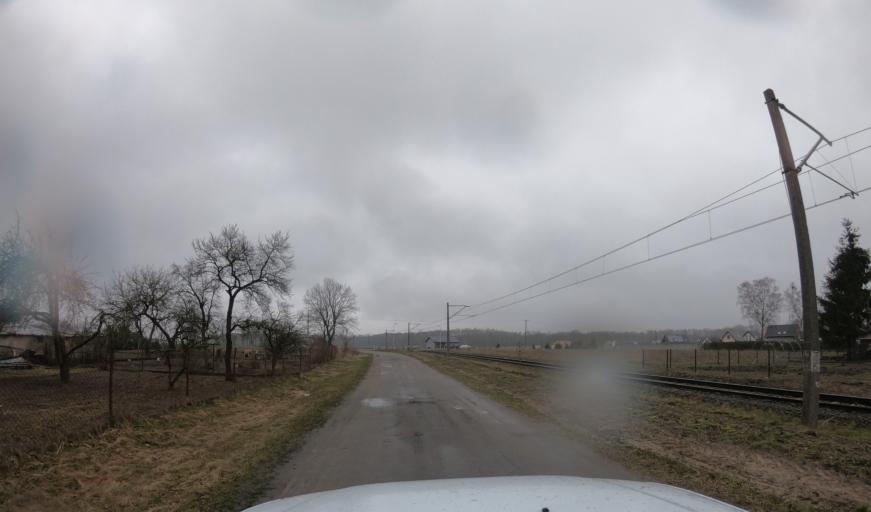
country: PL
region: West Pomeranian Voivodeship
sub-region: Powiat kamienski
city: Kamien Pomorski
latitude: 53.9013
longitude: 14.8239
